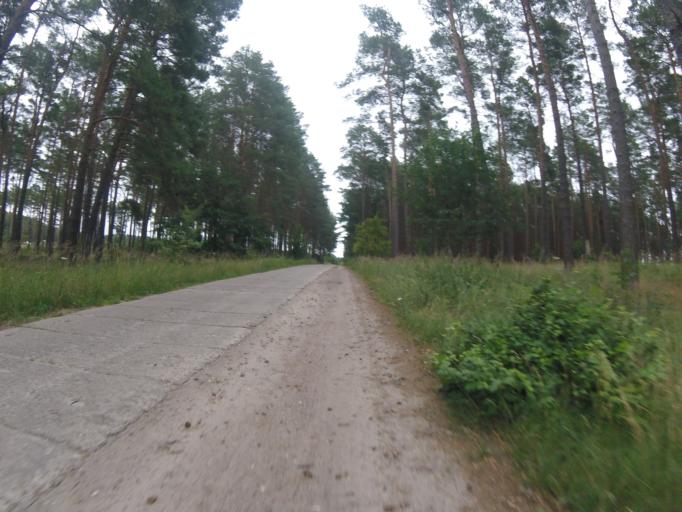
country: DE
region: Brandenburg
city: Schwerin
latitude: 52.1973
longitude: 13.6040
